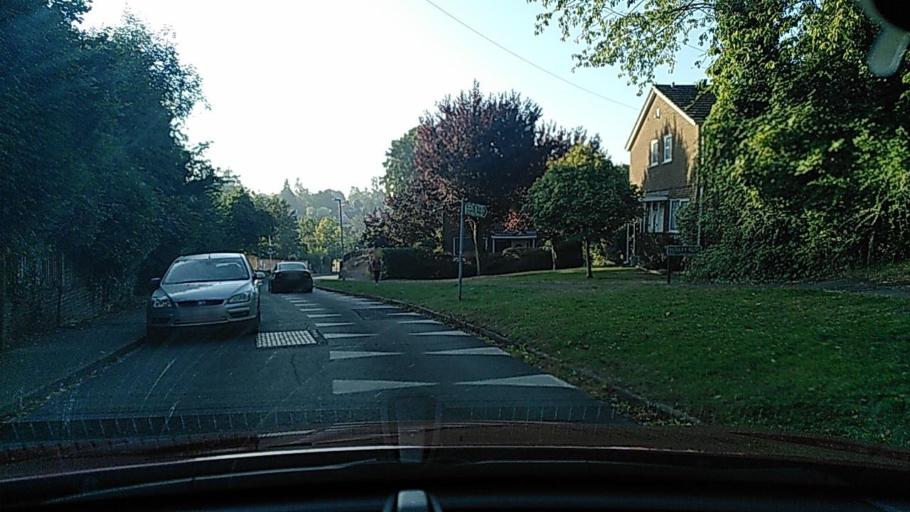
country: GB
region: England
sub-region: Reading
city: Reading
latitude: 51.4802
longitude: -0.9721
